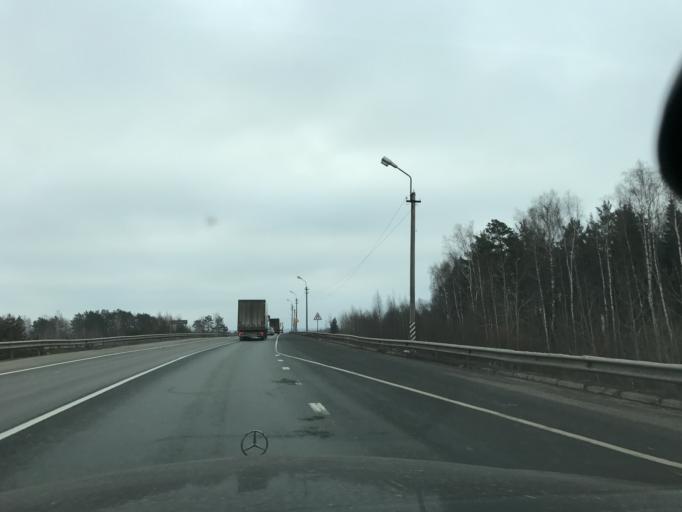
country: RU
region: Vladimir
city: Raduzhnyy
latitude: 56.0645
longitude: 40.3649
